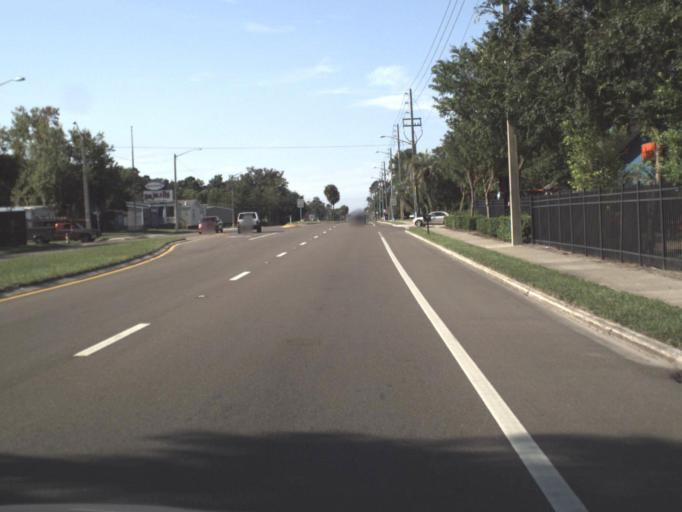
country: US
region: Florida
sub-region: Alachua County
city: Gainesville
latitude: 29.6966
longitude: -82.3391
